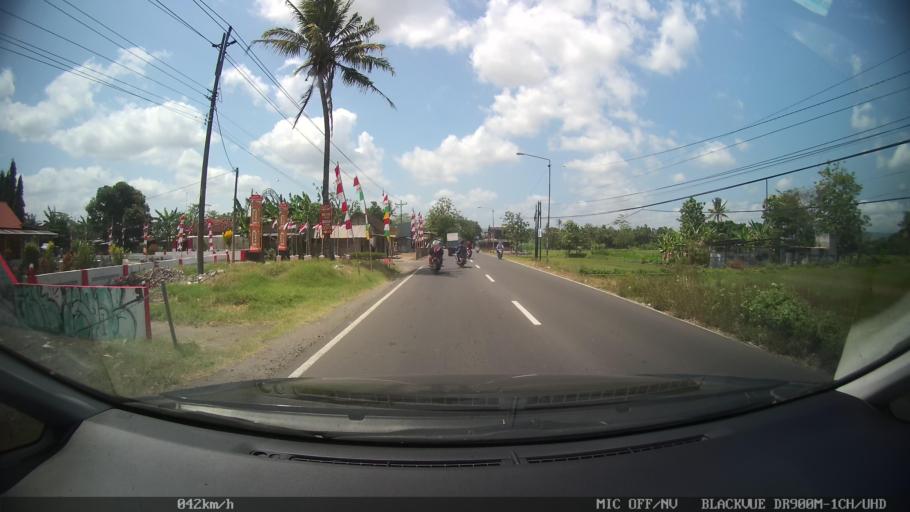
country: ID
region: Daerah Istimewa Yogyakarta
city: Bantul
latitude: -7.9047
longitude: 110.3344
